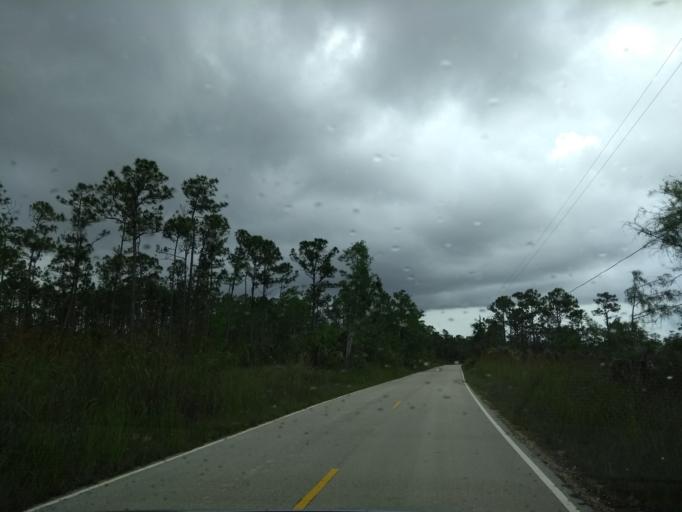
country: US
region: Florida
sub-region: Miami-Dade County
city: The Hammocks
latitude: 25.7534
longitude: -80.9338
